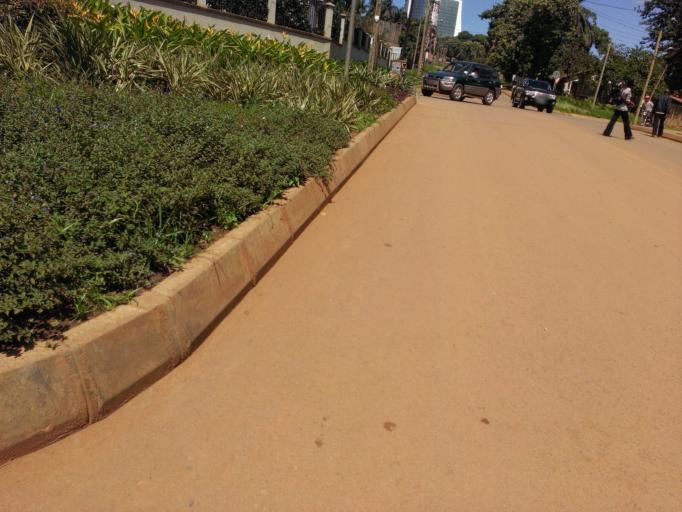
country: UG
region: Central Region
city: Kampala Central Division
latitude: 0.3285
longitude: 32.5749
